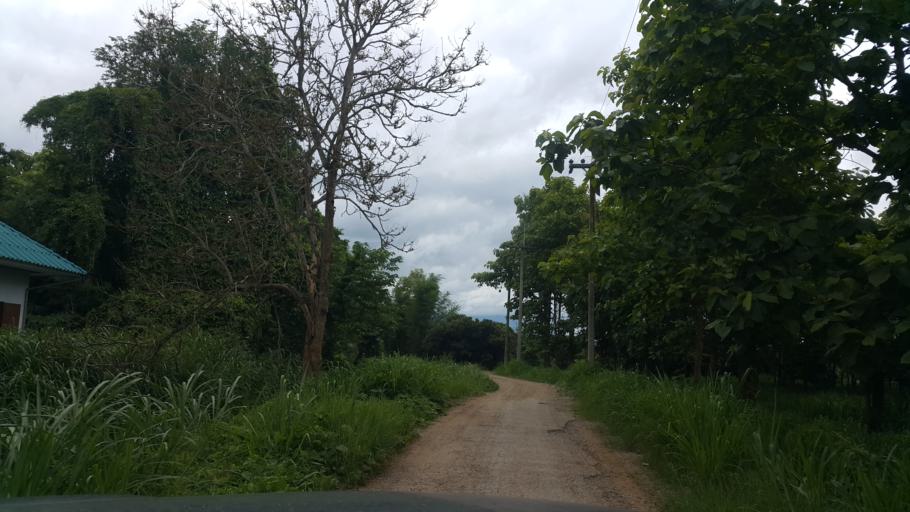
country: TH
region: Chiang Mai
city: Mae Taeng
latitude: 19.1933
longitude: 98.9841
